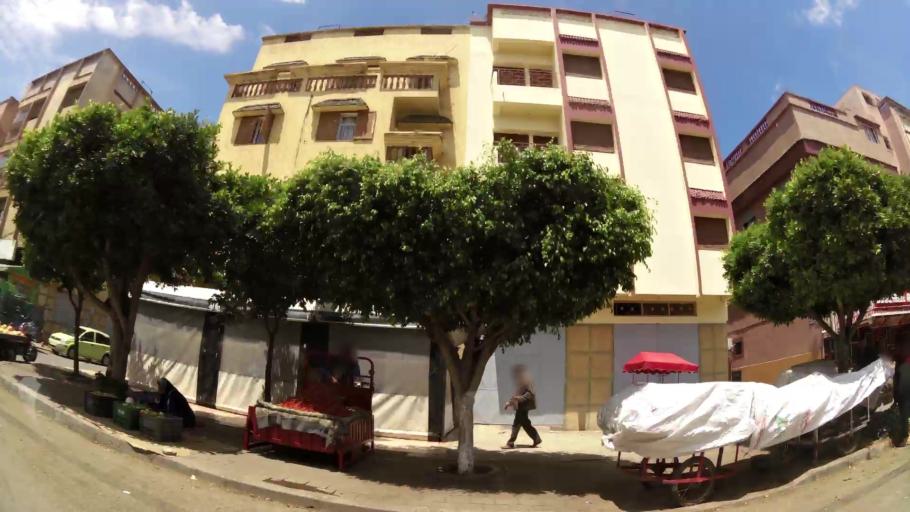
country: MA
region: Gharb-Chrarda-Beni Hssen
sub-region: Kenitra Province
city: Kenitra
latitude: 34.2698
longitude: -6.6016
